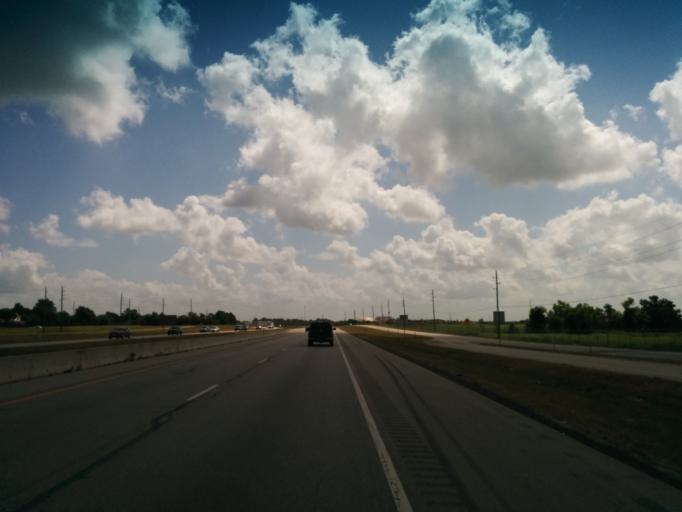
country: US
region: Texas
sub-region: Austin County
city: Sealy
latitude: 29.7664
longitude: -96.1459
